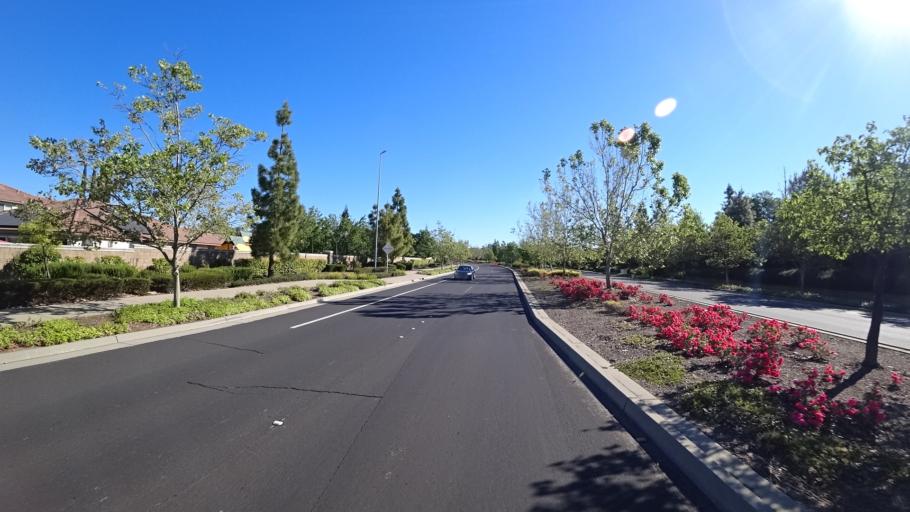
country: US
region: California
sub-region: Placer County
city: Roseville
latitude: 38.7931
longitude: -121.2782
